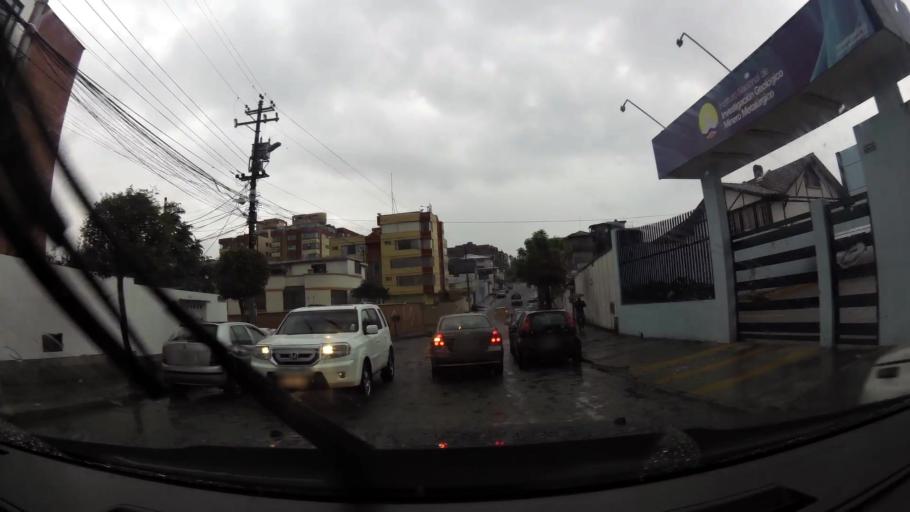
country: EC
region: Pichincha
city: Quito
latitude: -0.1568
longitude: -78.4641
